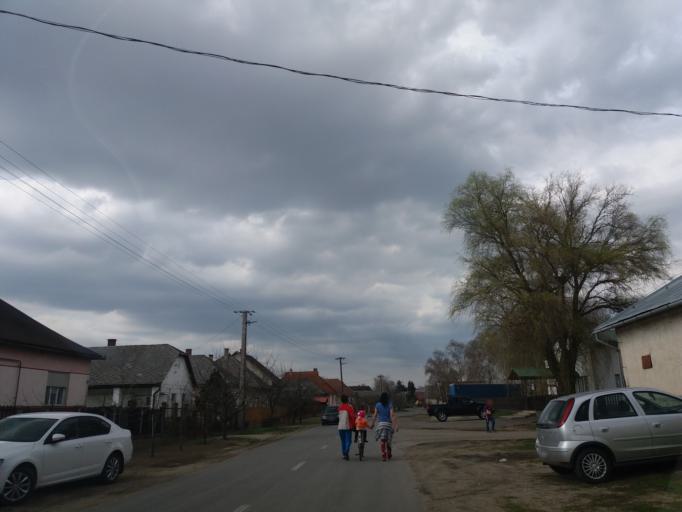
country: HU
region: Szabolcs-Szatmar-Bereg
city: Nyirtass
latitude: 48.1066
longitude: 22.0268
